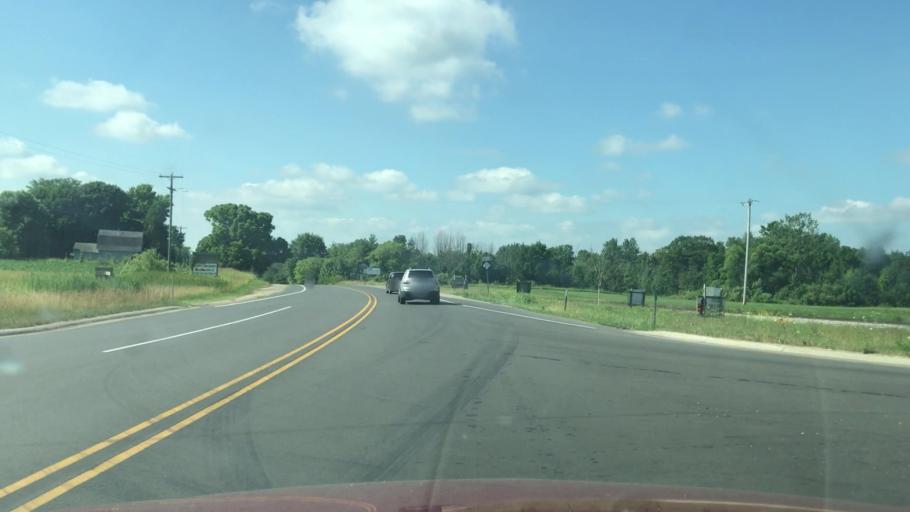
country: US
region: Michigan
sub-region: Newaygo County
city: Newaygo
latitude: 43.3512
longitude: -85.8112
